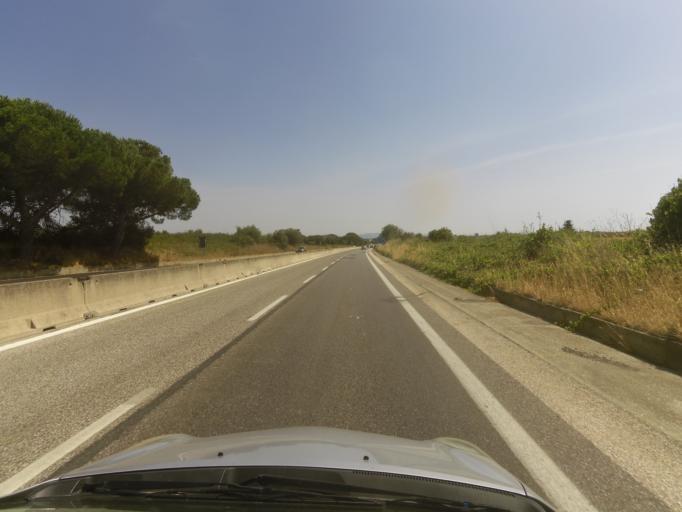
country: IT
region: Tuscany
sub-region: Provincia di Livorno
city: S.P. in Palazzi
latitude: 43.3385
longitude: 10.5229
